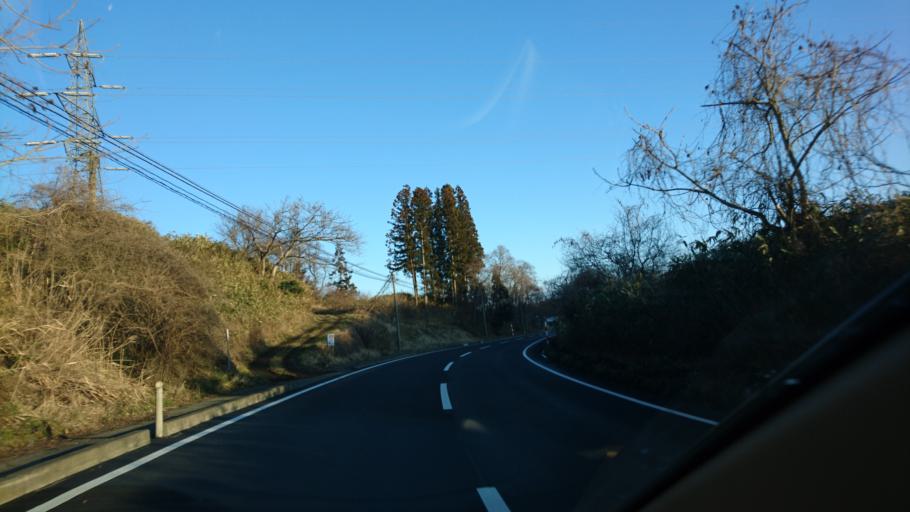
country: JP
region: Miyagi
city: Furukawa
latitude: 38.6560
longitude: 140.8910
